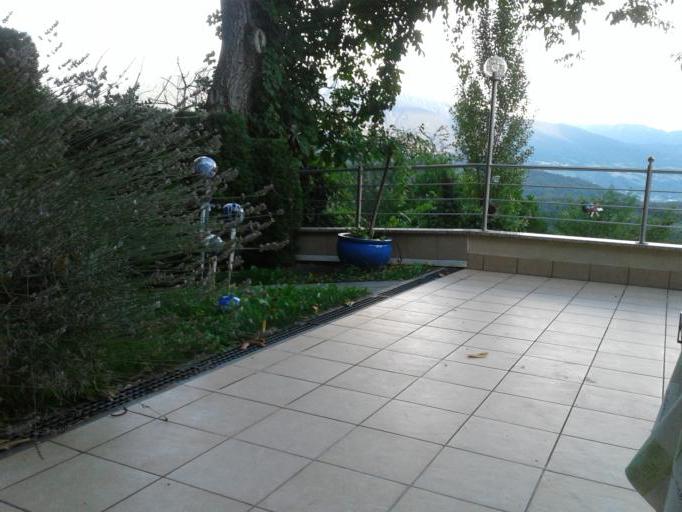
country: IT
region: Trentino-Alto Adige
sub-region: Bolzano
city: Naz-Sciaves - Natz-Schabs
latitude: 46.7804
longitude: 11.6385
